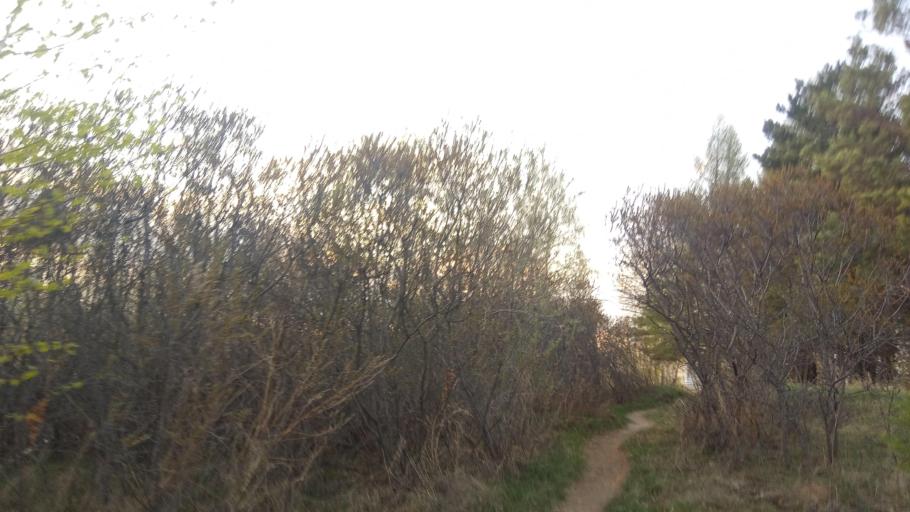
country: RU
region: Chelyabinsk
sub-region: Gorod Chelyabinsk
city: Chelyabinsk
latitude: 55.1620
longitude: 61.3127
